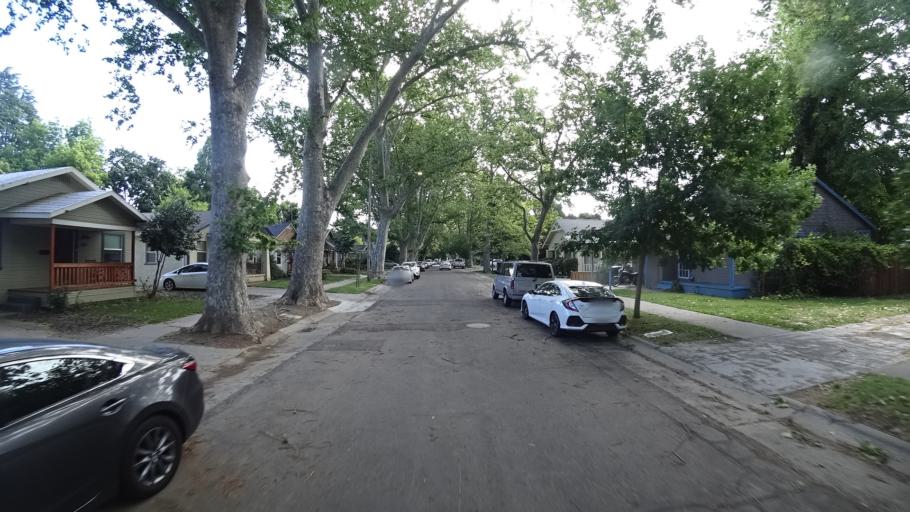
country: US
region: California
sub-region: Sacramento County
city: Sacramento
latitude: 38.5508
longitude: -121.5087
